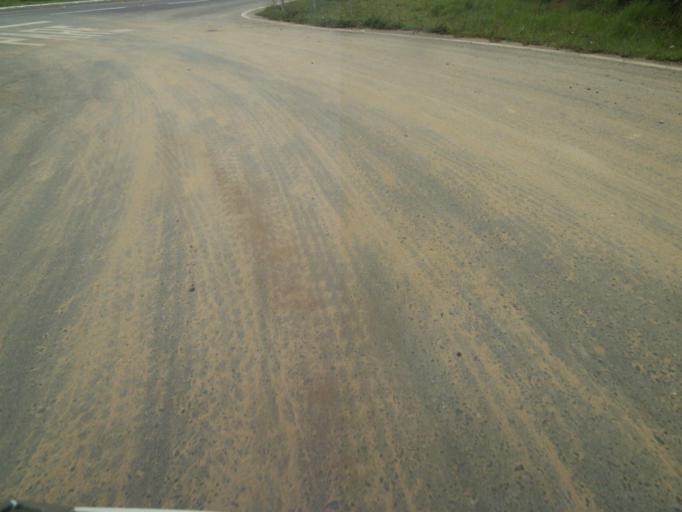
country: BR
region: Parana
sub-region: Palmeira
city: Palmeira
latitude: -25.4450
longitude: -49.9592
